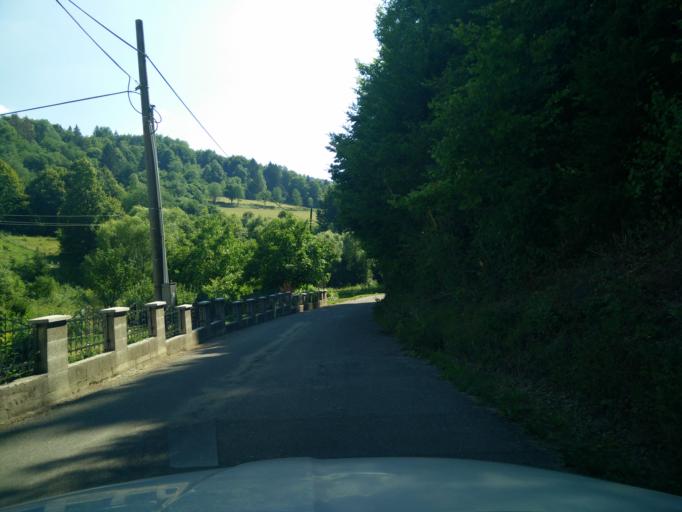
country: SK
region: Nitriansky
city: Bojnice
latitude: 48.9110
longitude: 18.4865
